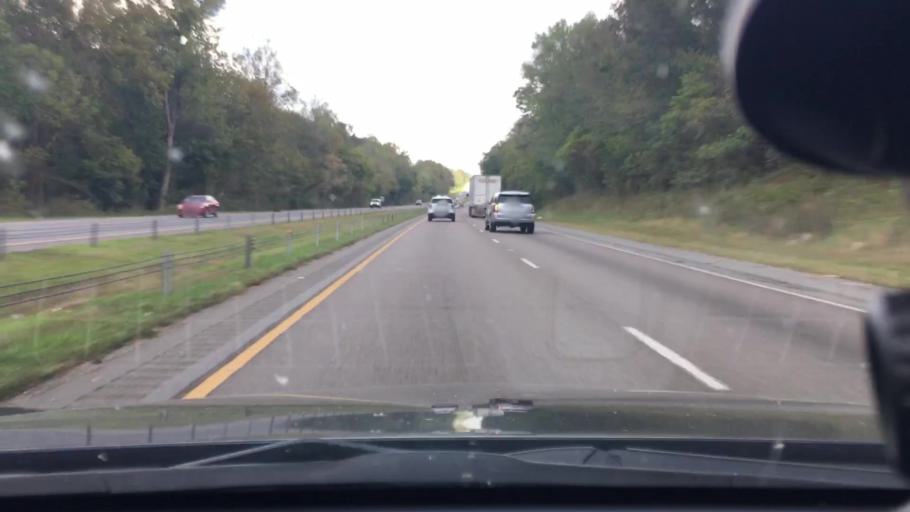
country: US
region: North Carolina
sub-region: Alexander County
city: Stony Point
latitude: 35.7569
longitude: -81.0414
